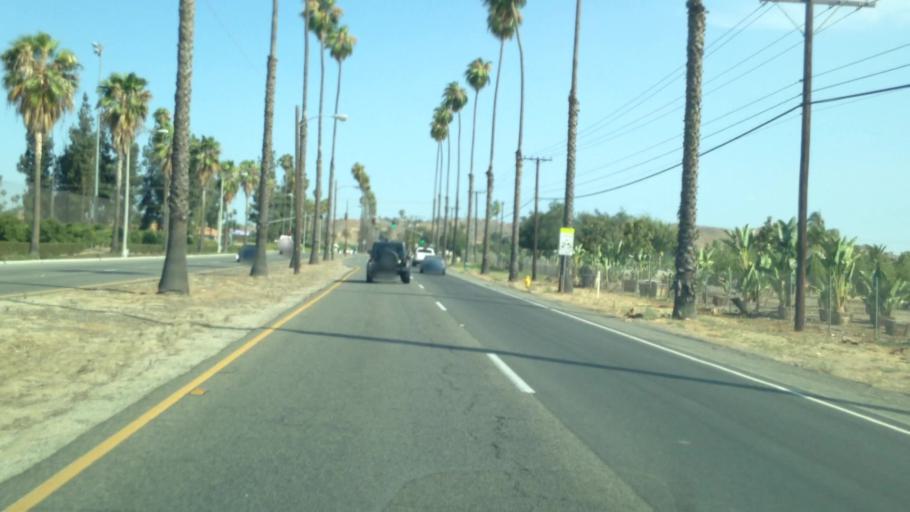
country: US
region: California
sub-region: Riverside County
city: Riverside
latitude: 33.9030
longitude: -117.4324
